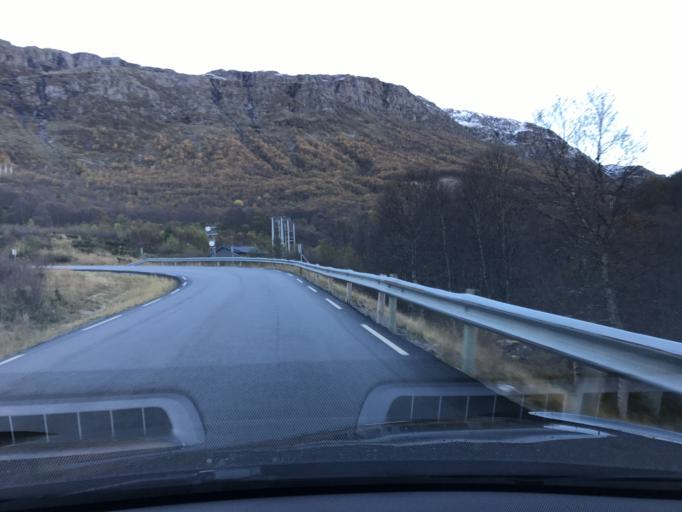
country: NO
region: Sogn og Fjordane
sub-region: Aurland
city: Aurlandsvangen
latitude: 60.8483
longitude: 7.3100
